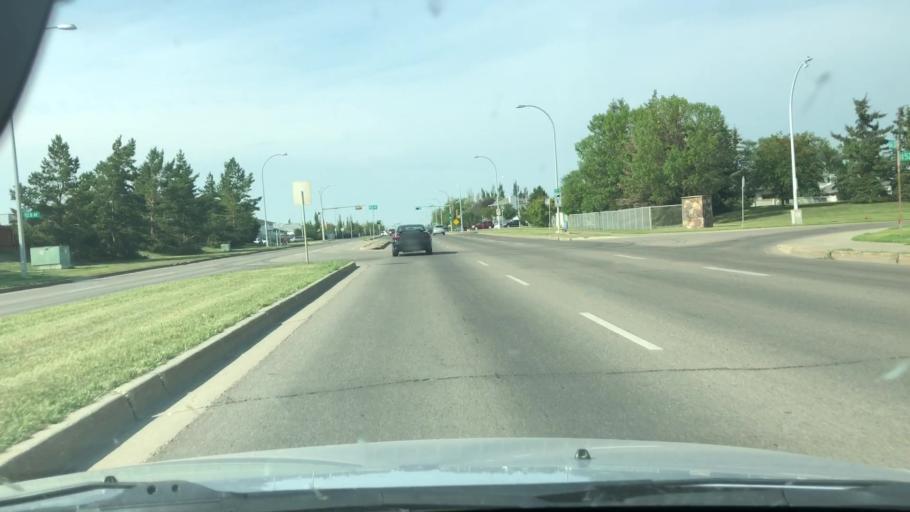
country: CA
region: Alberta
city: Edmonton
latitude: 53.6142
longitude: -113.4428
